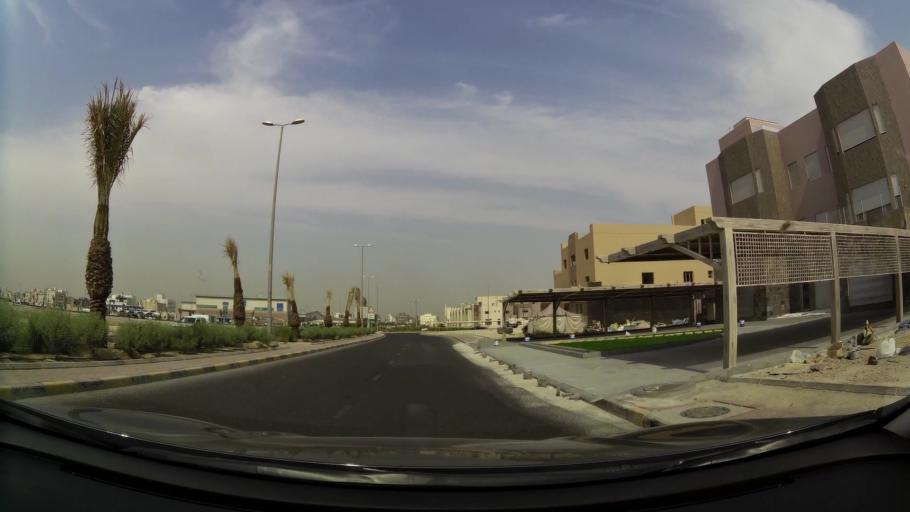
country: KW
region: Al Farwaniyah
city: Janub as Surrah
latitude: 29.2887
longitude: 47.9932
